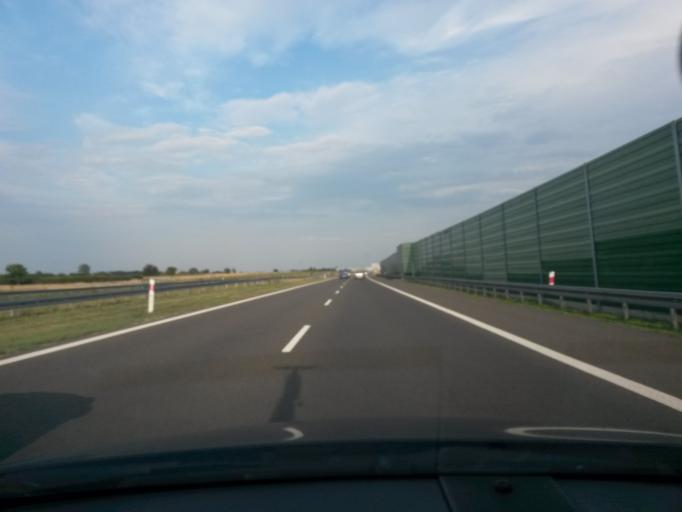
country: PL
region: Lodz Voivodeship
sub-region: Powiat zgierski
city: Strykow
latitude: 51.8973
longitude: 19.5297
